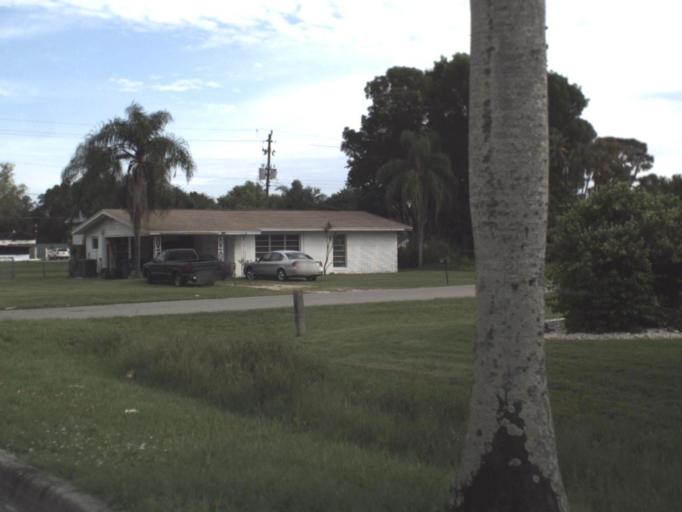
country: US
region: Florida
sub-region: Lee County
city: Harlem Heights
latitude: 26.4983
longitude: -81.9434
